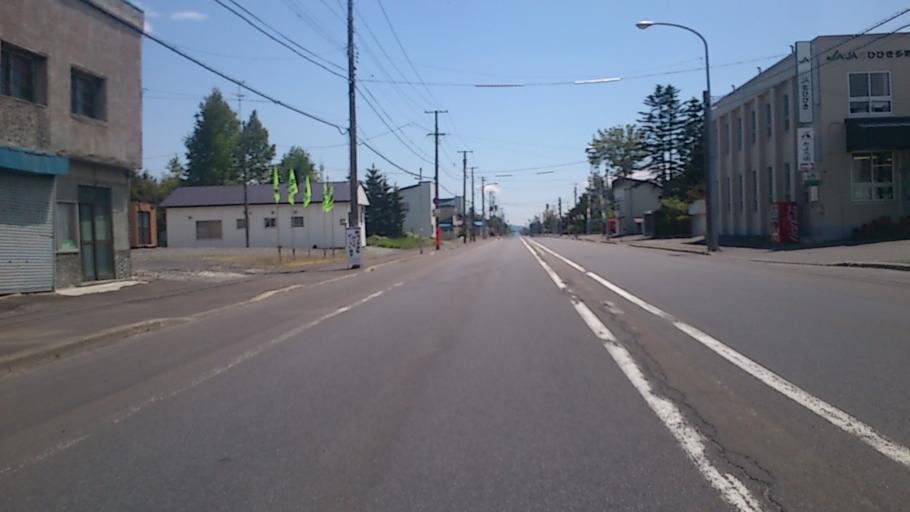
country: JP
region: Hokkaido
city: Nayoro
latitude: 44.2405
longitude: 142.3949
